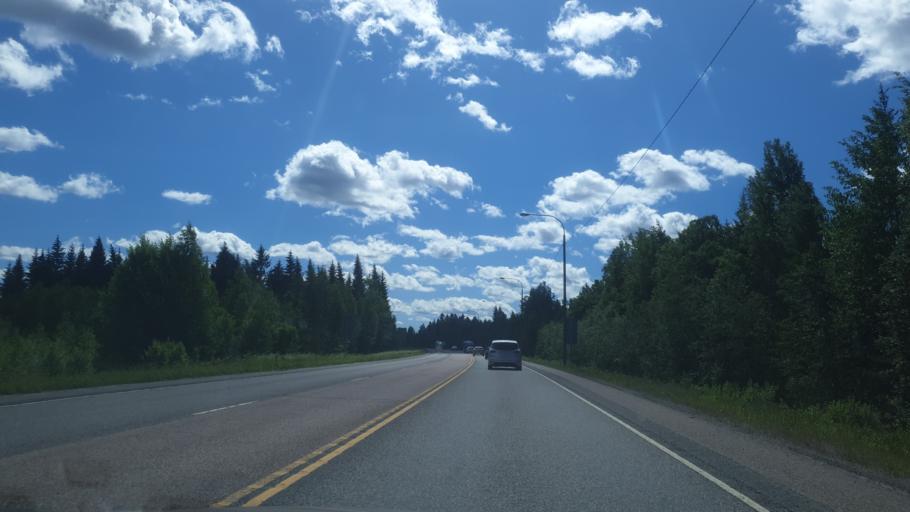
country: FI
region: Northern Savo
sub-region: Varkaus
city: Varkaus
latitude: 62.3623
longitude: 27.8099
